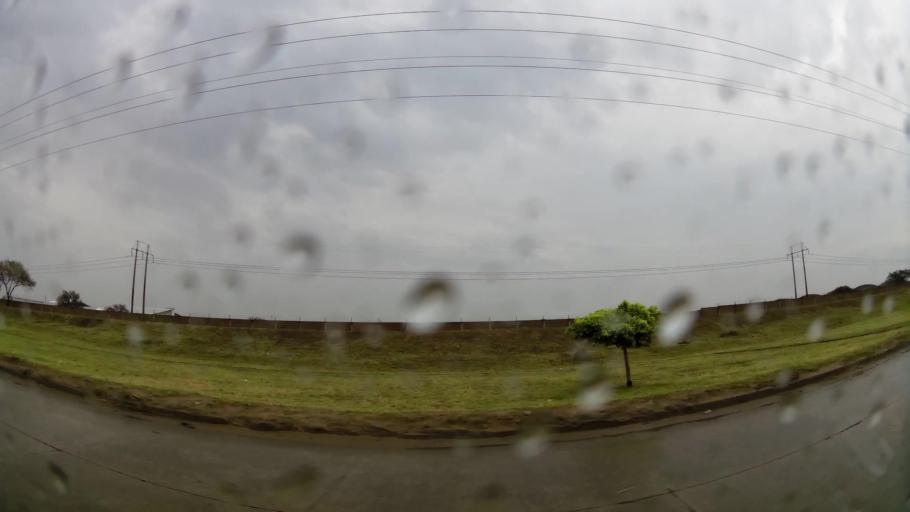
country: BO
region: Santa Cruz
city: Santa Cruz de la Sierra
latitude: -17.7607
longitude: -63.1284
